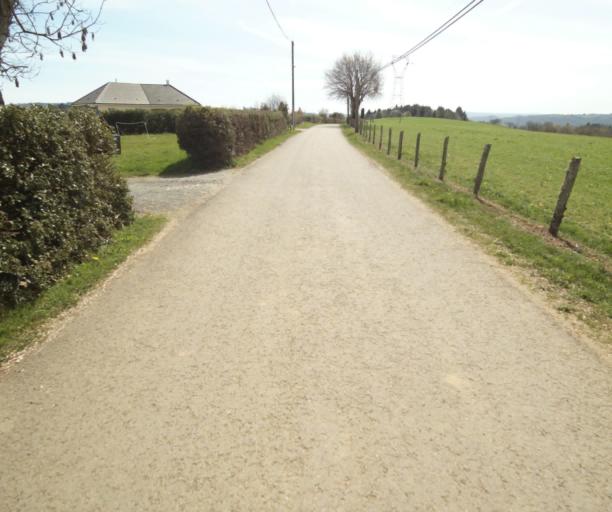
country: FR
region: Limousin
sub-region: Departement de la Correze
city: Naves
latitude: 45.3691
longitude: 1.8025
